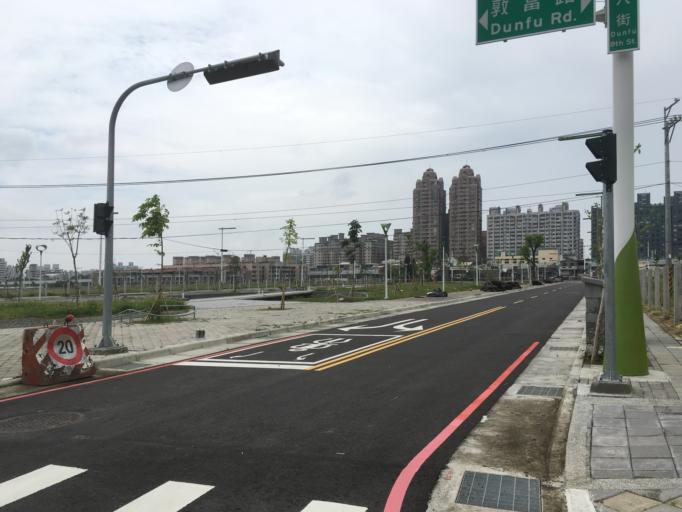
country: TW
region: Taiwan
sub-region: Taichung City
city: Taichung
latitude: 24.1897
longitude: 120.7069
